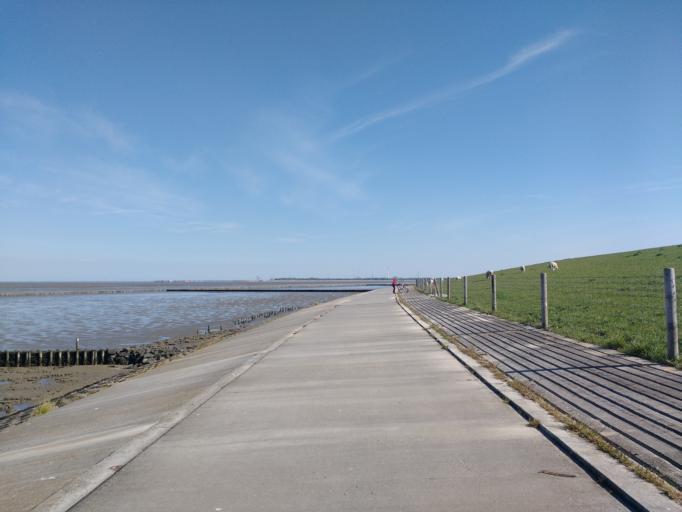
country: DE
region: Lower Saxony
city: Schillig
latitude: 53.6799
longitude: 8.0242
